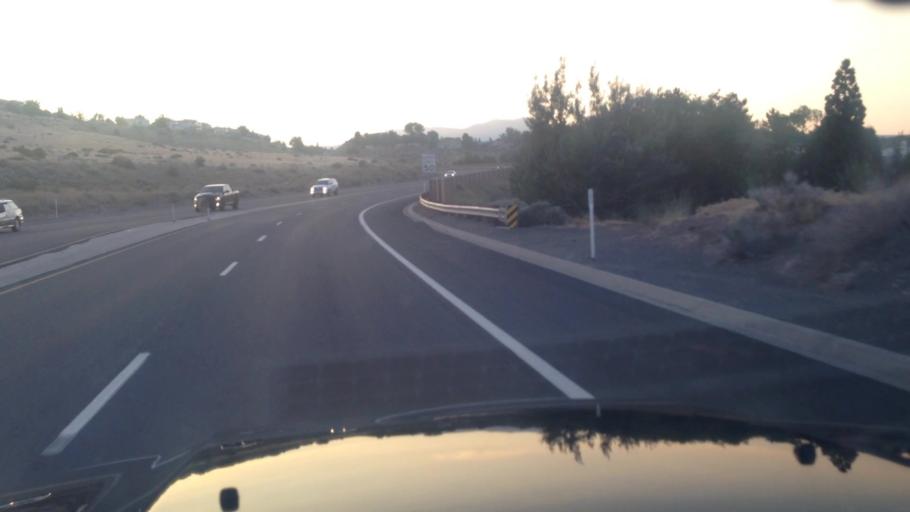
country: US
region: Nevada
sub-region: Washoe County
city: Reno
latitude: 39.4777
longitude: -119.8448
